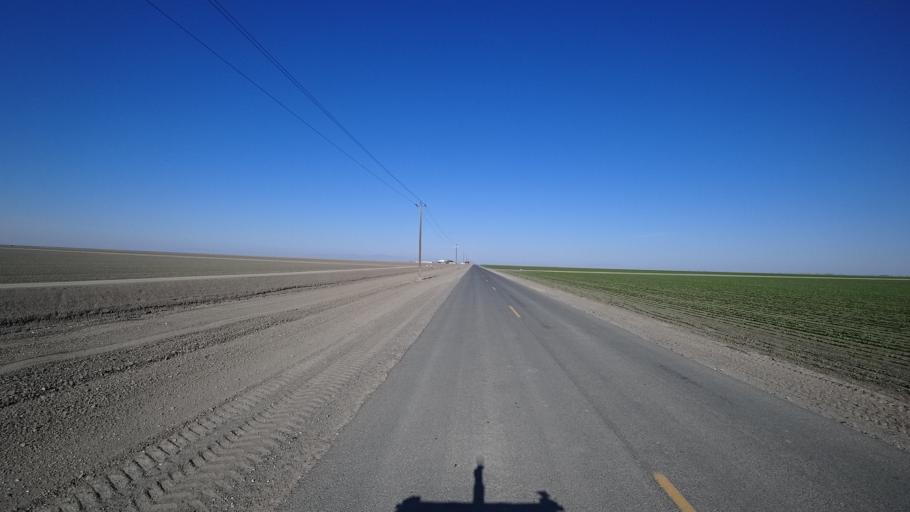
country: US
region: California
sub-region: Kings County
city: Corcoran
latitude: 36.0797
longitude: -119.6690
